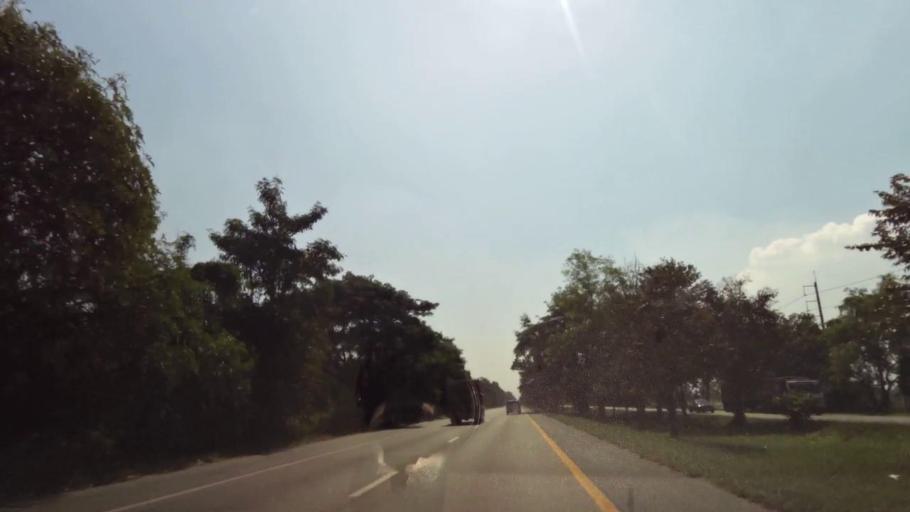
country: TH
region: Phichit
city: Wachira Barami
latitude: 16.5793
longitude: 100.1478
